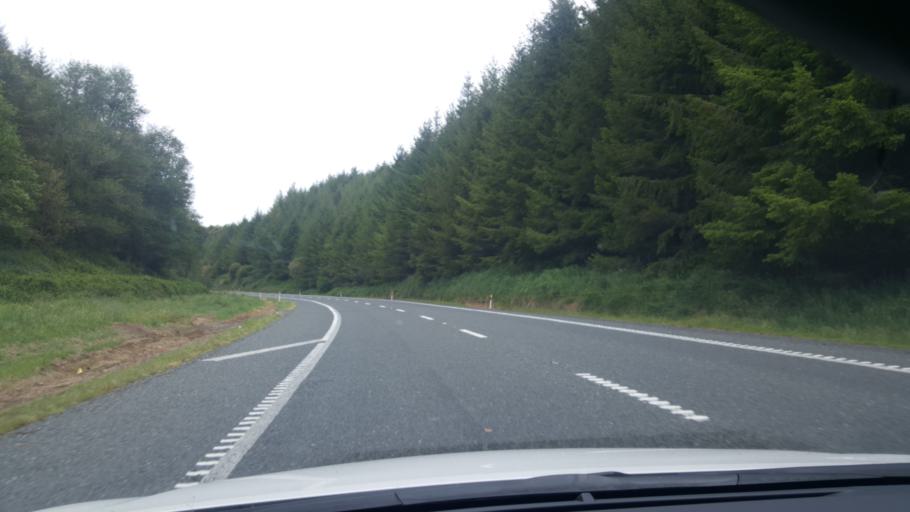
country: NZ
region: Bay of Plenty
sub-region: Rotorua District
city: Rotorua
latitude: -38.2381
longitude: 176.3012
